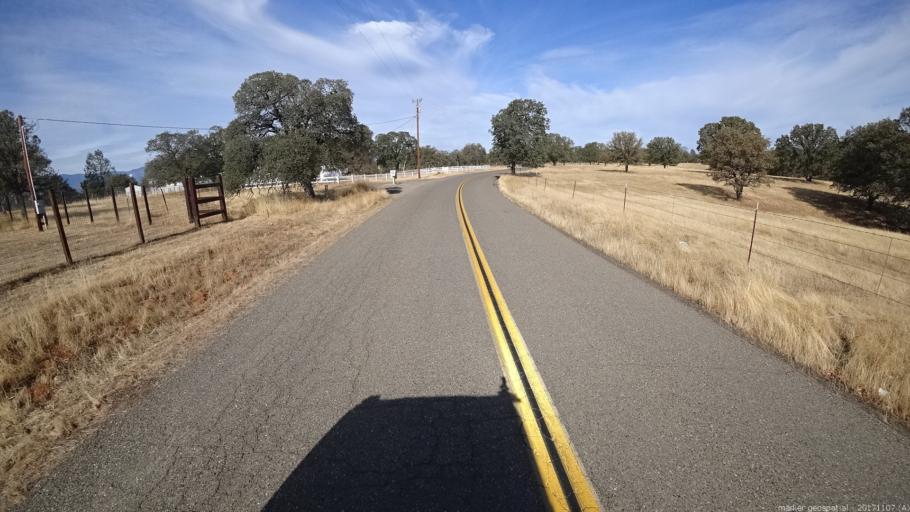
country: US
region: California
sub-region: Shasta County
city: Shasta
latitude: 40.4198
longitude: -122.5245
